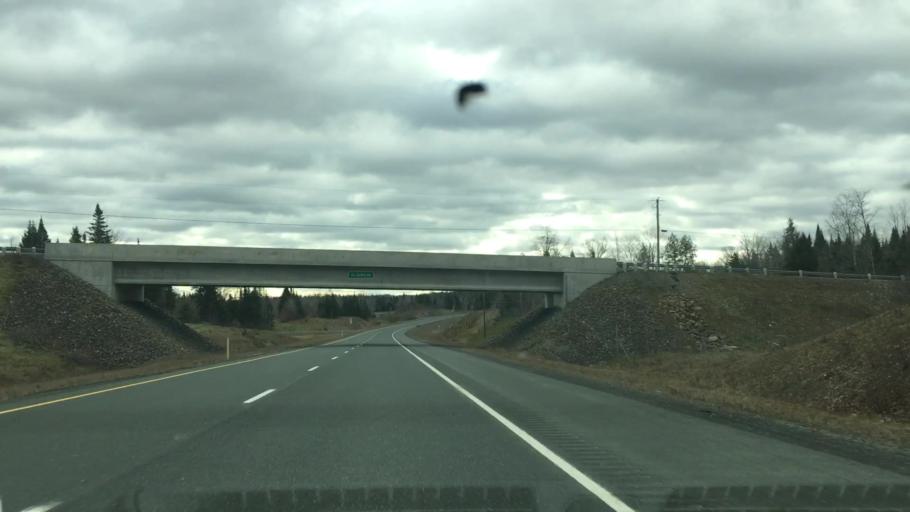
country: US
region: Maine
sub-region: Aroostook County
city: Easton
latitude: 46.6263
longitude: -67.7400
